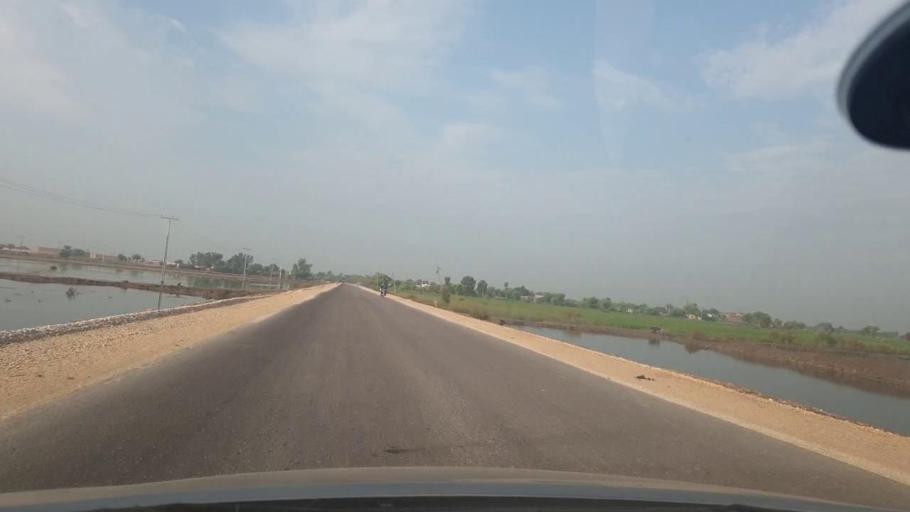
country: PK
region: Sindh
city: Jacobabad
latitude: 28.2198
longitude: 68.3726
